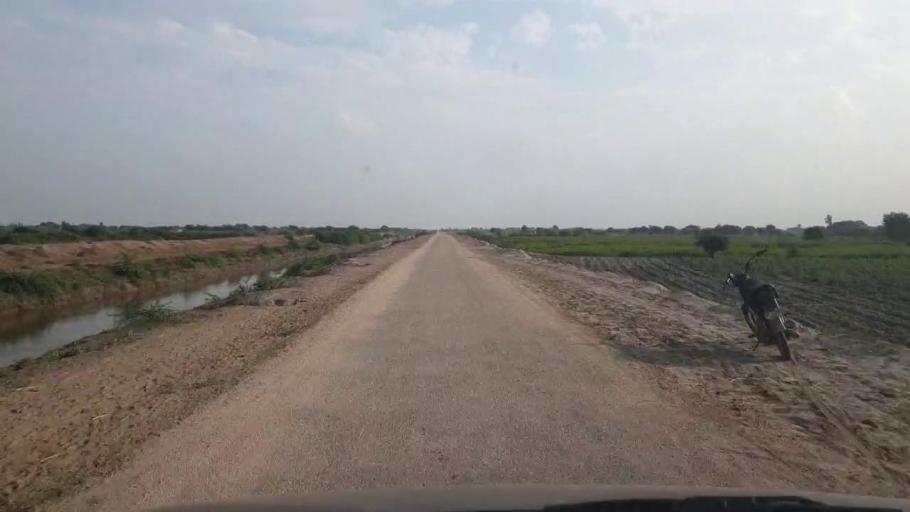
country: PK
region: Sindh
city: Badin
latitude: 24.5438
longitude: 68.6730
